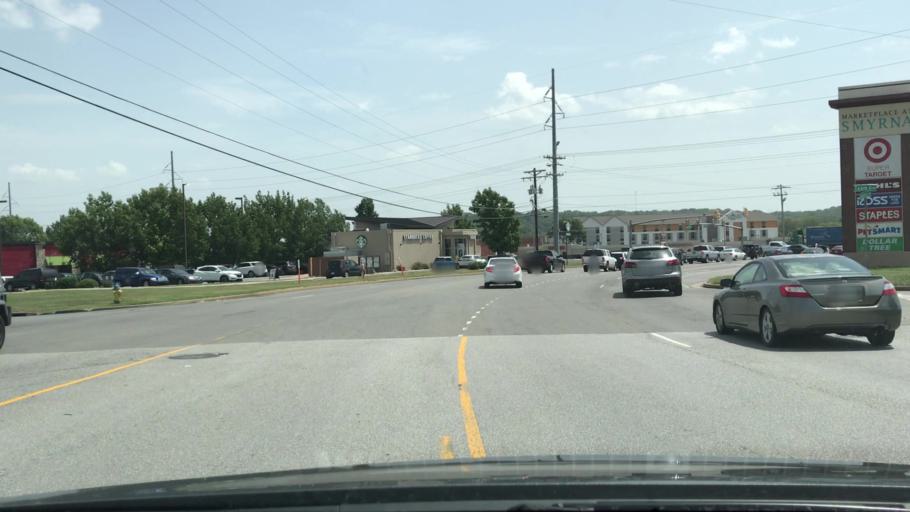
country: US
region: Tennessee
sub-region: Rutherford County
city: La Vergne
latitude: 35.9790
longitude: -86.5643
